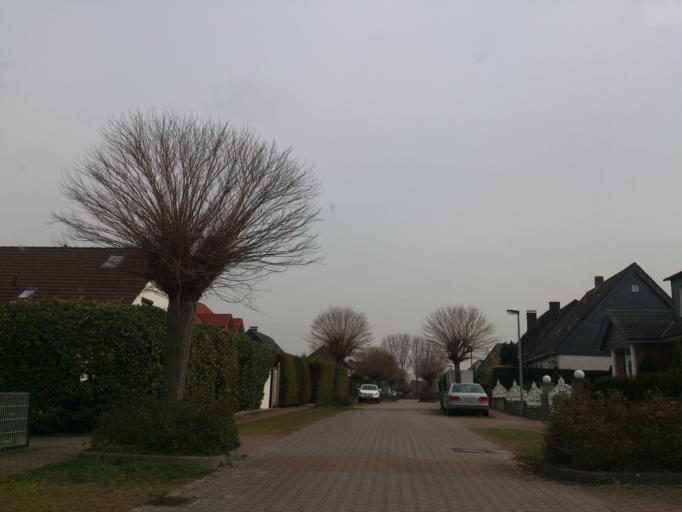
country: DE
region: North Rhine-Westphalia
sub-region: Regierungsbezirk Arnsberg
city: Soest
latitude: 51.5517
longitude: 8.0548
